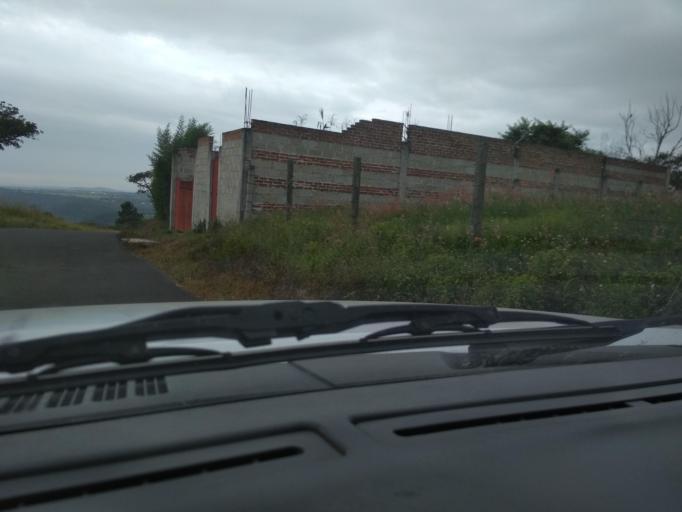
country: MX
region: Veracruz
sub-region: Emiliano Zapata
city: Dos Rios
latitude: 19.5165
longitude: -96.7929
